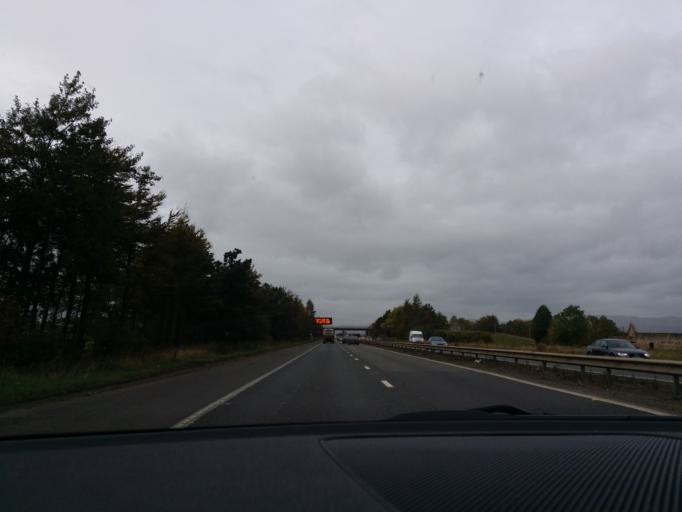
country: GB
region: Scotland
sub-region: Falkirk
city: Falkirk
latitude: 56.0263
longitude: -3.7607
